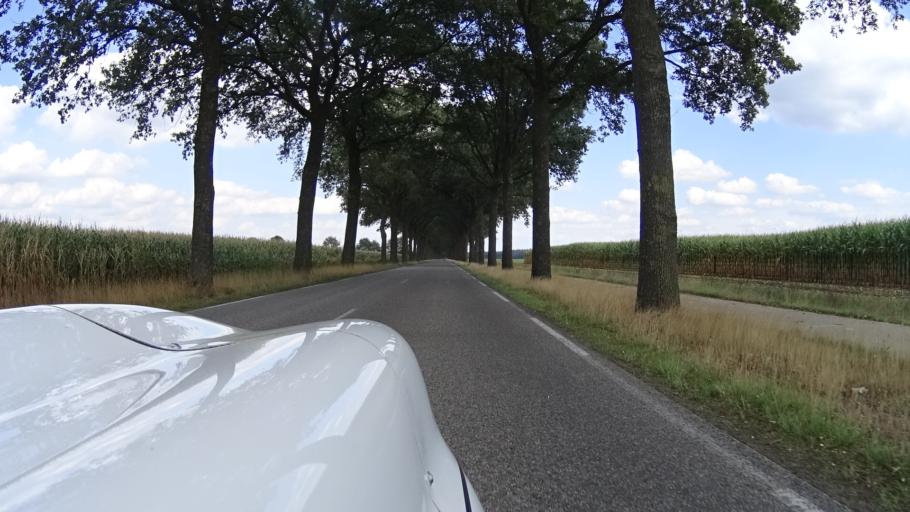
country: NL
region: North Brabant
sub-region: Gemeente Mill en Sint Hubert
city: Wilbertoord
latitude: 51.6235
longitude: 5.8001
